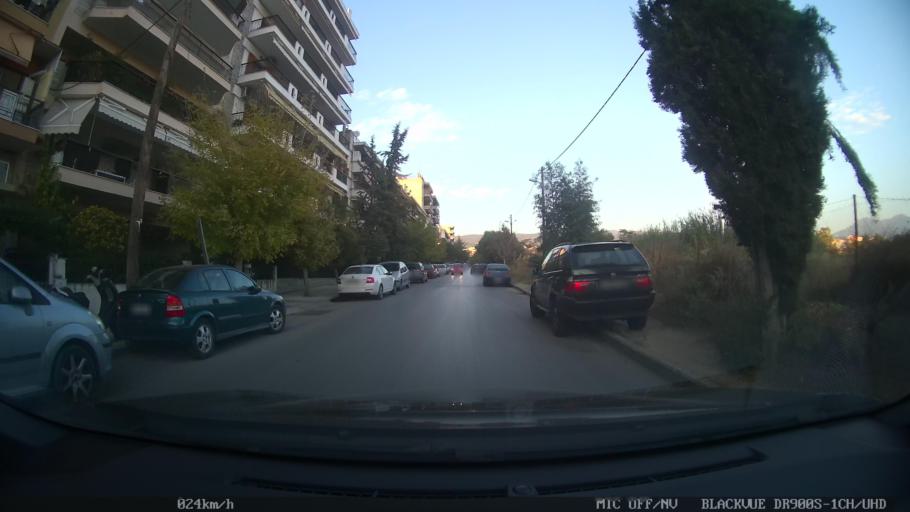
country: GR
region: Central Macedonia
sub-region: Nomos Thessalonikis
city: Pylaia
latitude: 40.6054
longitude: 22.9840
